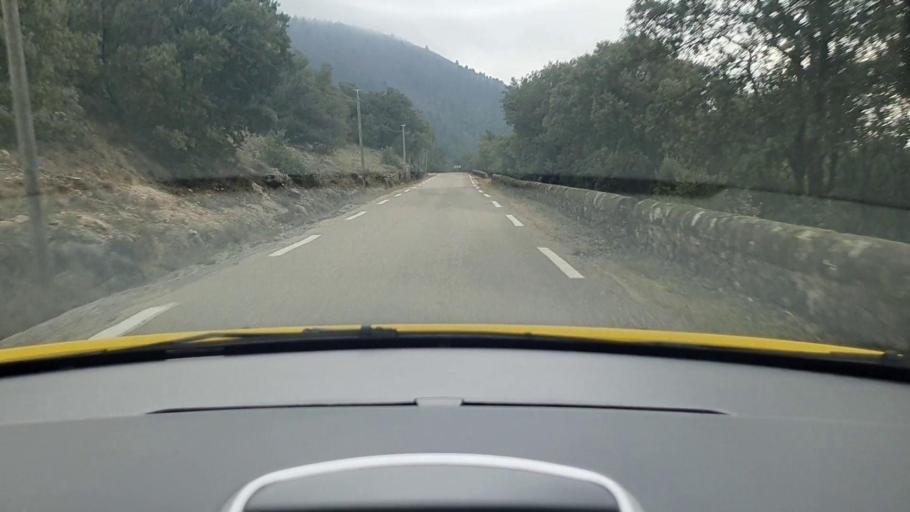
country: FR
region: Languedoc-Roussillon
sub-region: Departement du Gard
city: Besseges
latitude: 44.3454
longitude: 4.0293
